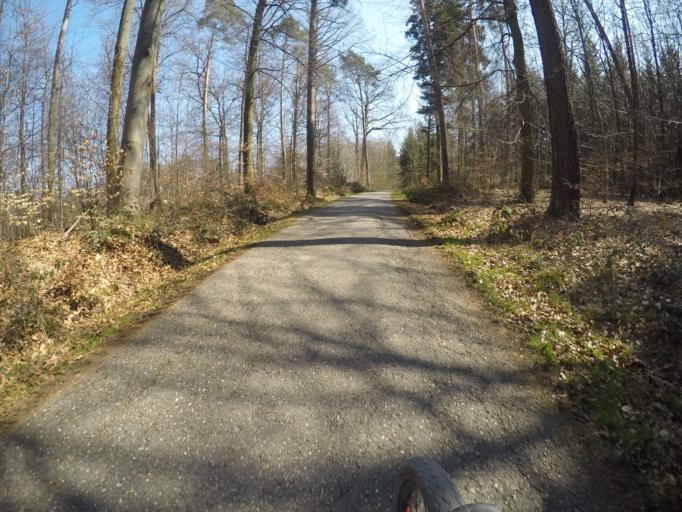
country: DE
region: Baden-Wuerttemberg
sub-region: Regierungsbezirk Stuttgart
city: Sindelfingen
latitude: 48.7296
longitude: 9.0518
